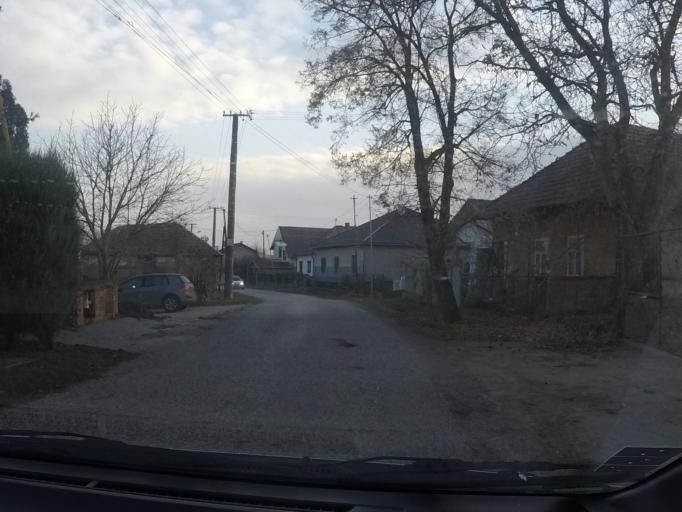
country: SK
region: Nitriansky
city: Zeliezovce
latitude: 48.1040
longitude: 18.5306
